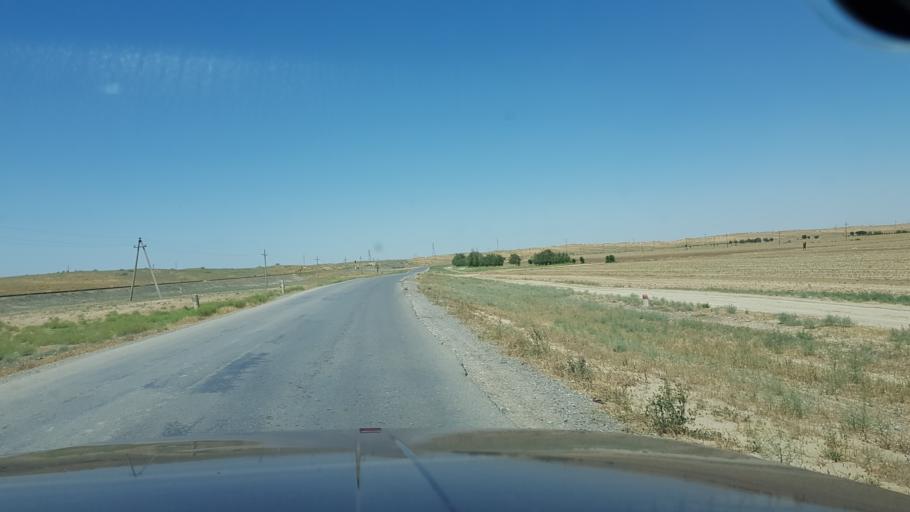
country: TM
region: Ahal
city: Annau
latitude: 37.8502
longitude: 58.7131
